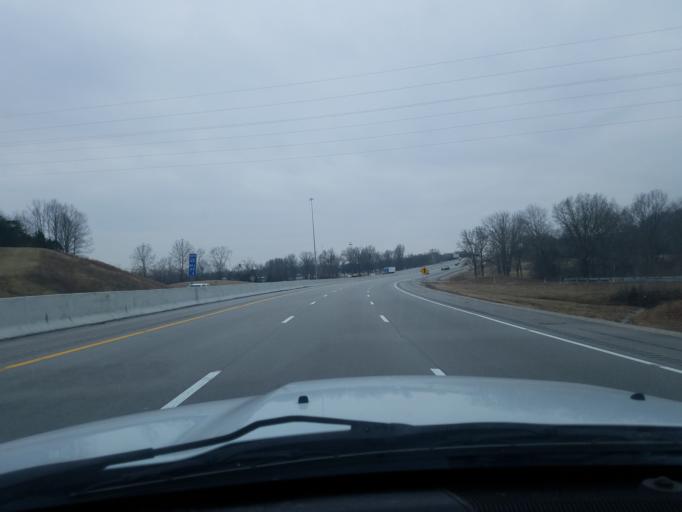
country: US
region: Kentucky
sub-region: Hart County
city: Munfordville
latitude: 37.2960
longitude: -85.9014
